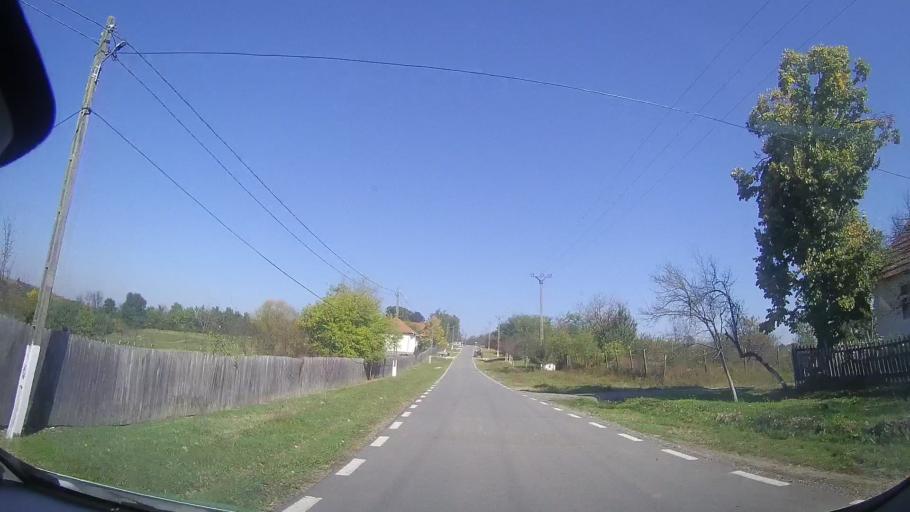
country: RO
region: Timis
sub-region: Comuna Ohaba Lunga
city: Ohaba Lunga
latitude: 45.9044
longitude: 21.9362
